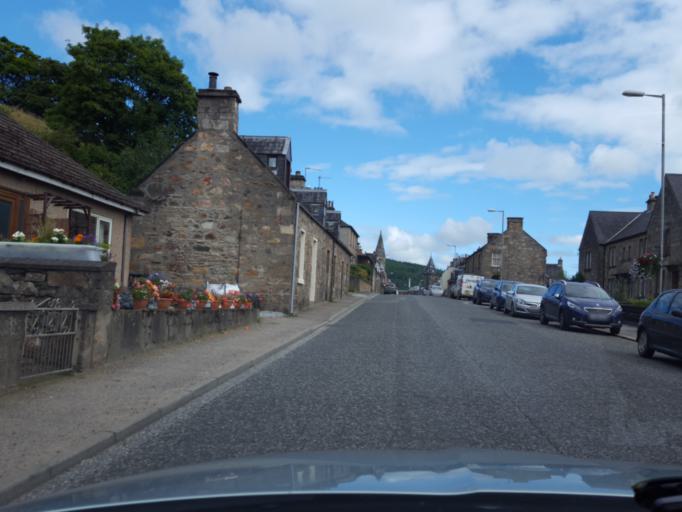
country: GB
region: Scotland
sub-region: Moray
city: Rothes
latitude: 57.5245
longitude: -3.2084
